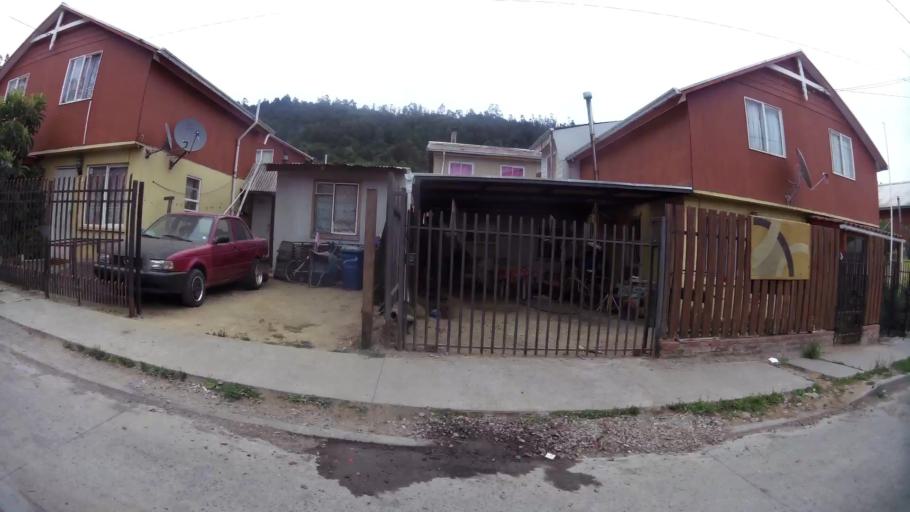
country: CL
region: Biobio
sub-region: Provincia de Concepcion
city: Concepcion
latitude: -36.8342
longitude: -73.0108
